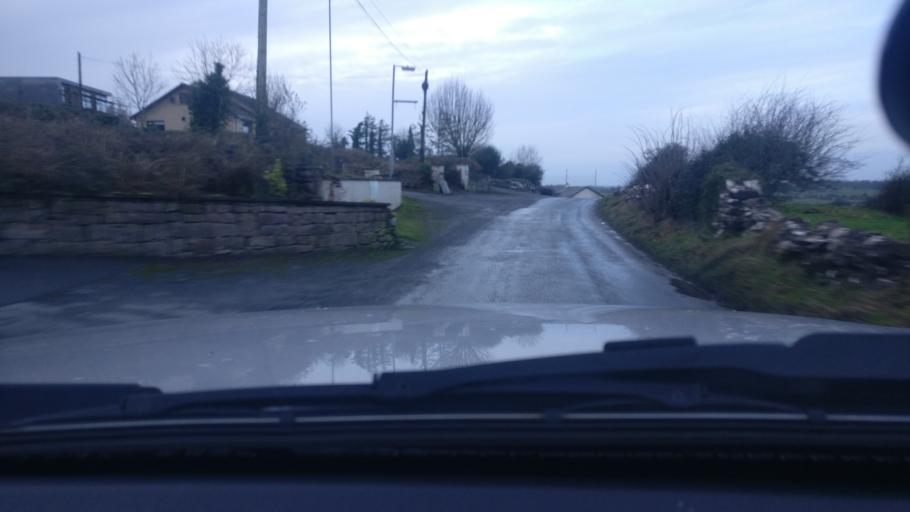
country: IE
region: Connaught
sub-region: County Galway
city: Loughrea
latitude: 53.1636
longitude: -8.5562
